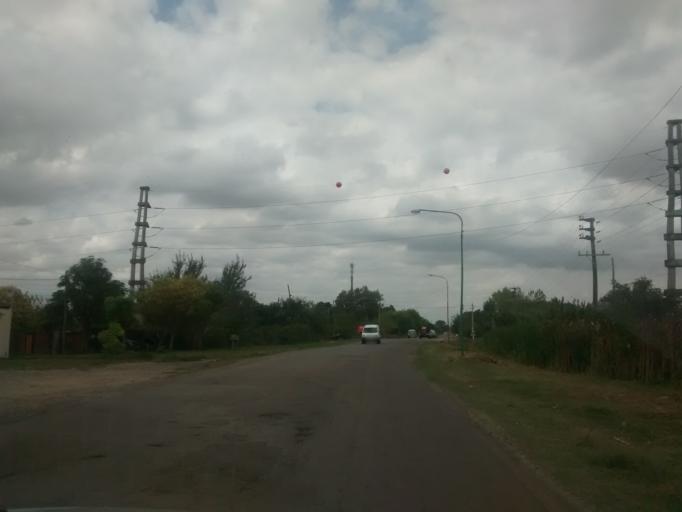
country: AR
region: Buenos Aires
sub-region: Partido de La Plata
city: La Plata
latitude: -34.9720
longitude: -57.9425
